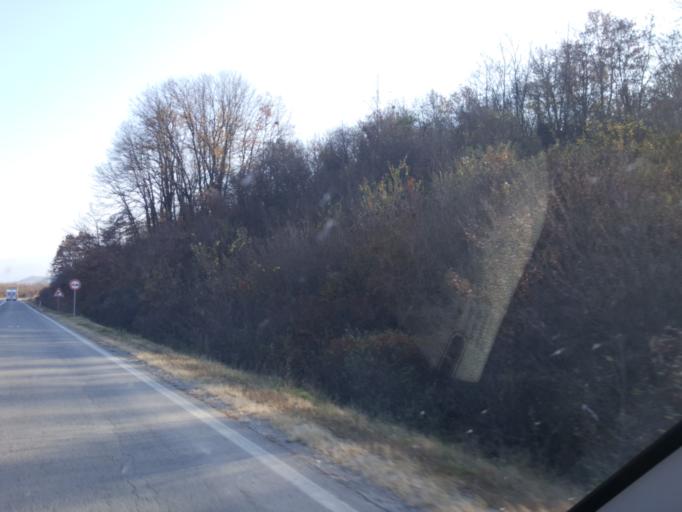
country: RS
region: Central Serbia
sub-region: Pirotski Okrug
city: Bela Palanka
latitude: 43.2900
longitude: 22.2161
